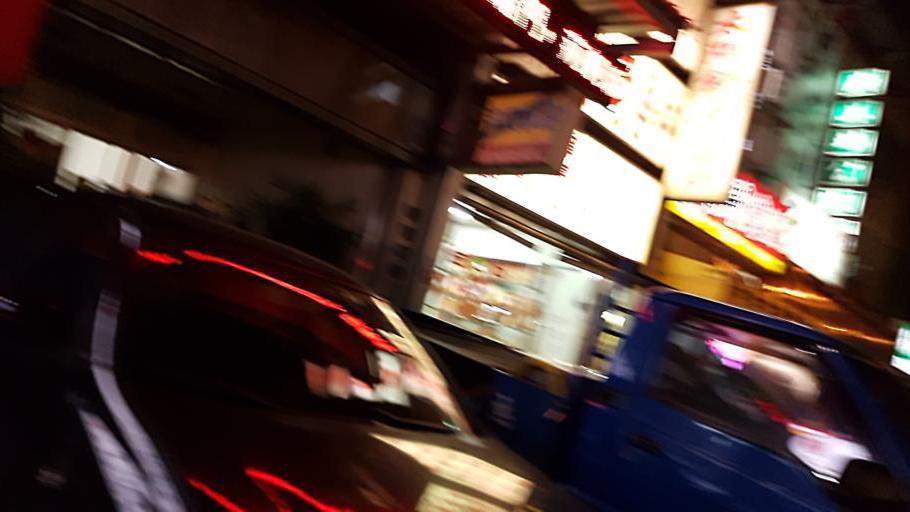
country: TW
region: Taiwan
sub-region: Changhua
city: Chang-hua
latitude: 24.0687
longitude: 120.5263
